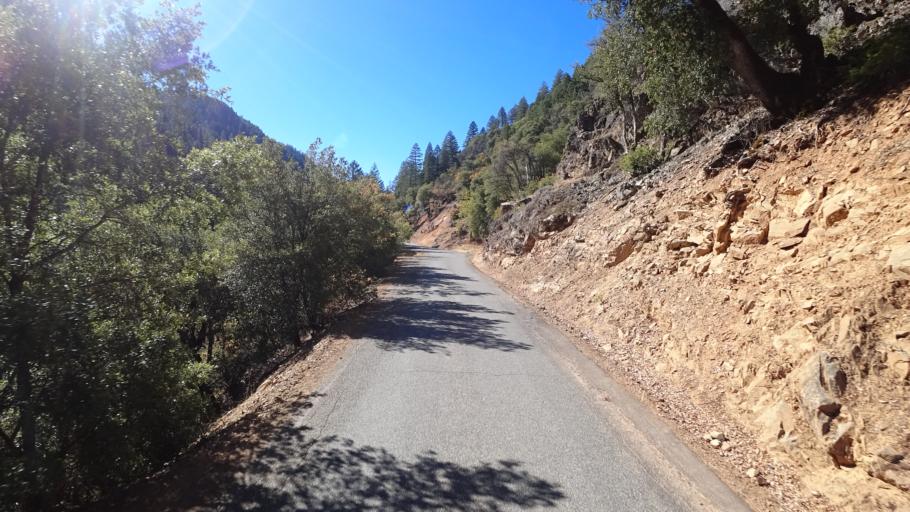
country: US
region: California
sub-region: Siskiyou County
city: Happy Camp
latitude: 41.2974
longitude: -123.0906
